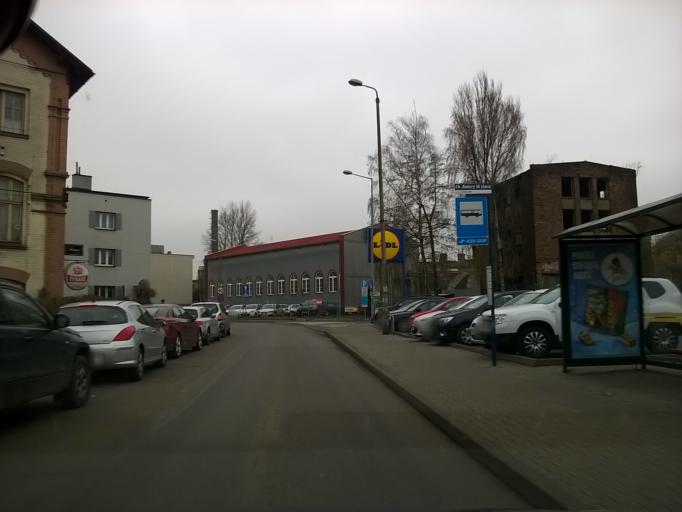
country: PL
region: Silesian Voivodeship
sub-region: Swietochlowice
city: Swietochlowice
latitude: 50.2764
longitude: 18.9403
